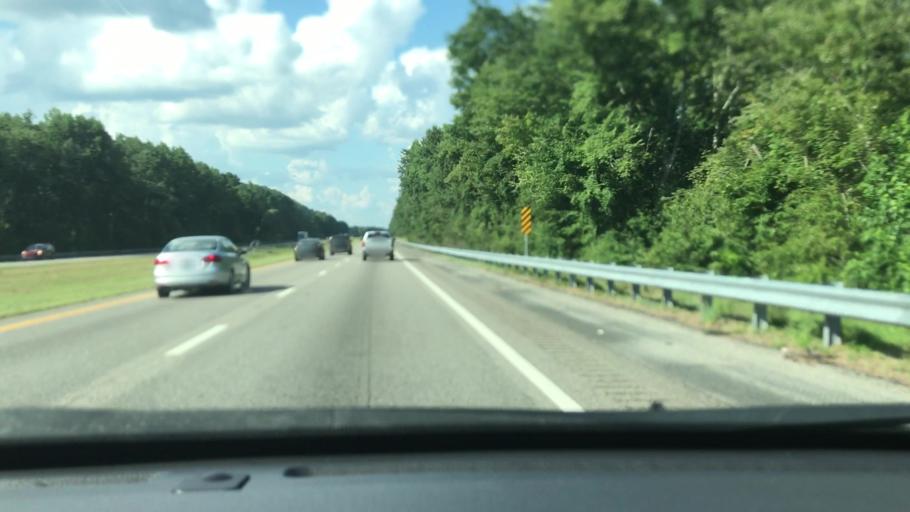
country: US
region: South Carolina
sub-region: Sumter County
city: East Sumter
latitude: 33.9344
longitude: -80.0666
